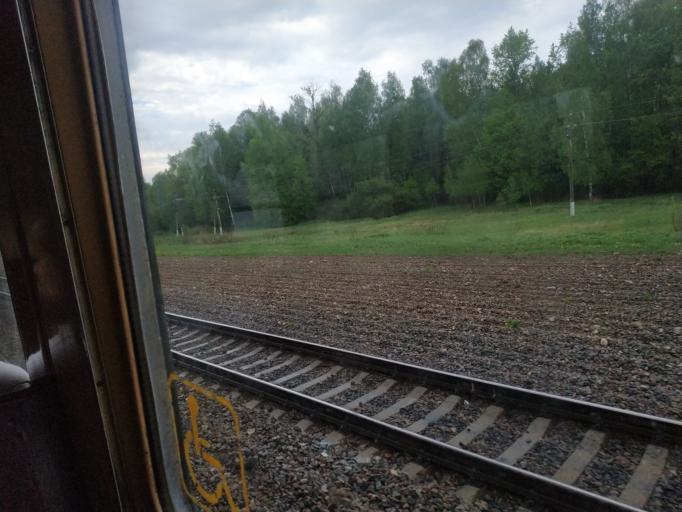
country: RU
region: Kaluga
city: Baryatino
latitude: 54.3531
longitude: 34.3220
